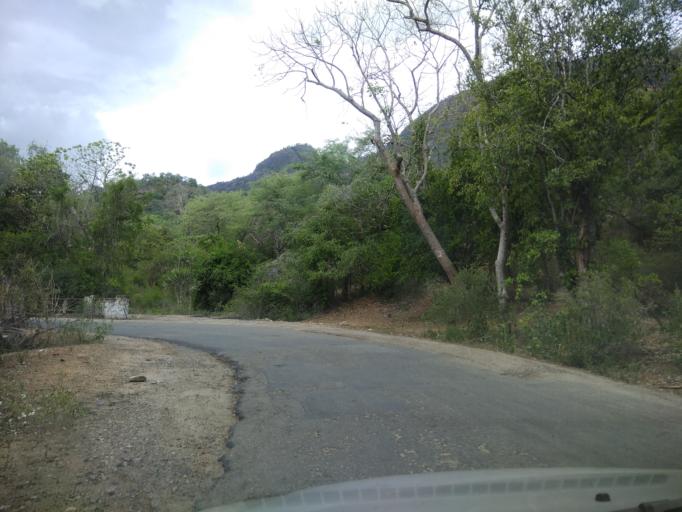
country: IN
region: Tamil Nadu
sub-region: Tiruppur
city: Dhali
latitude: 10.3317
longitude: 77.2140
